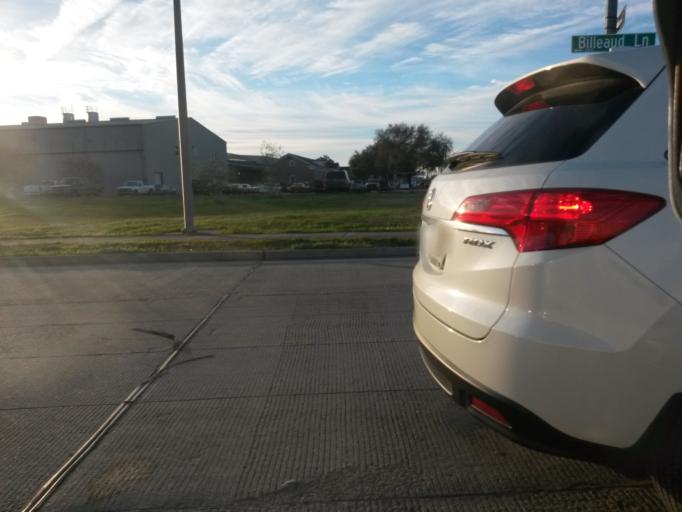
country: US
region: Louisiana
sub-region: Lafayette Parish
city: Lafayette
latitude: 30.2225
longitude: -92.0520
